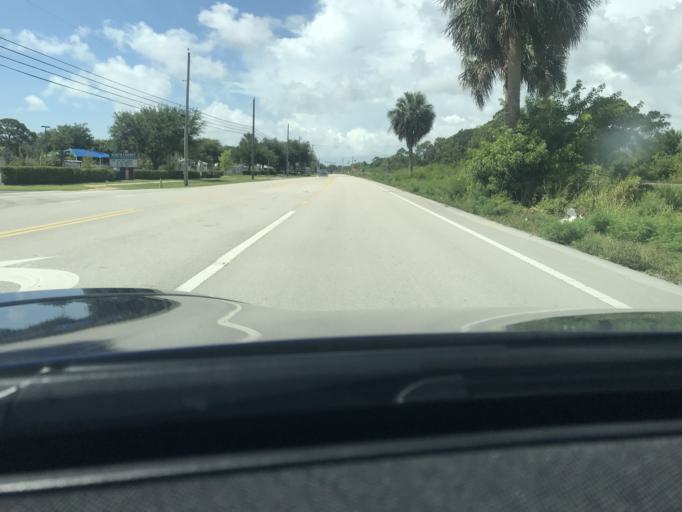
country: US
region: Florida
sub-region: Indian River County
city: Winter Beach
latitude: 27.7148
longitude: -80.4213
